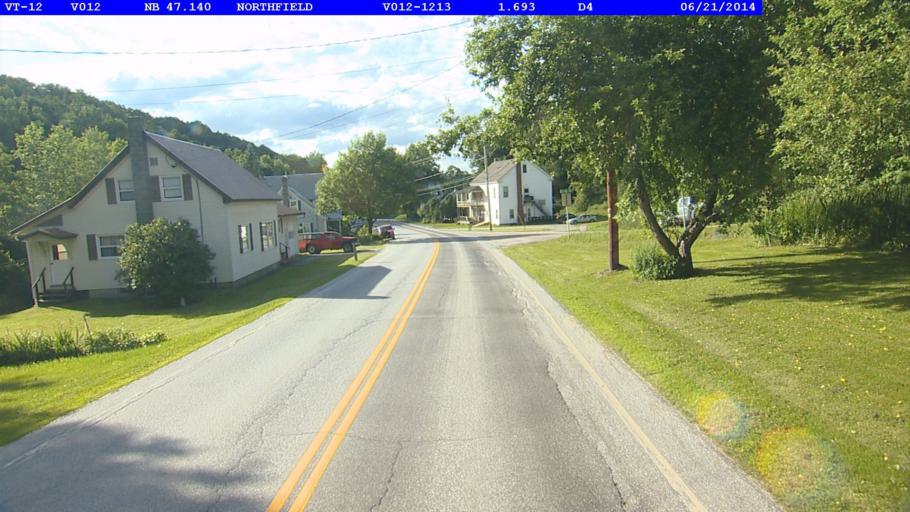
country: US
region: Vermont
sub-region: Washington County
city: Northfield
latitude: 44.1141
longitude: -72.6530
